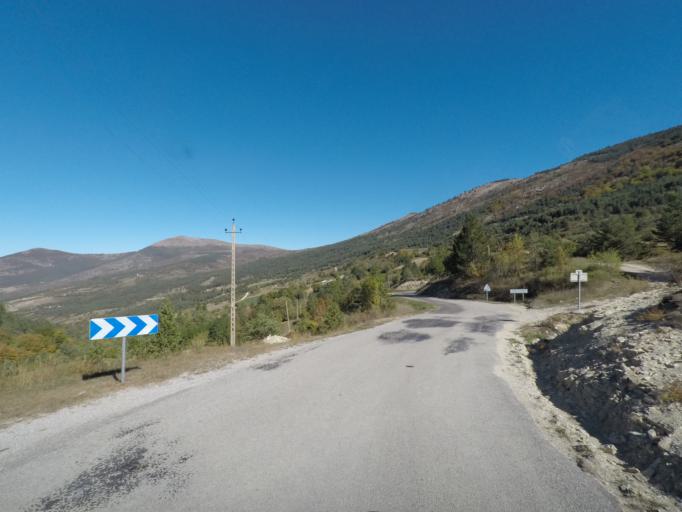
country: FR
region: Rhone-Alpes
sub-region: Departement de la Drome
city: Die
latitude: 44.5399
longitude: 5.3689
